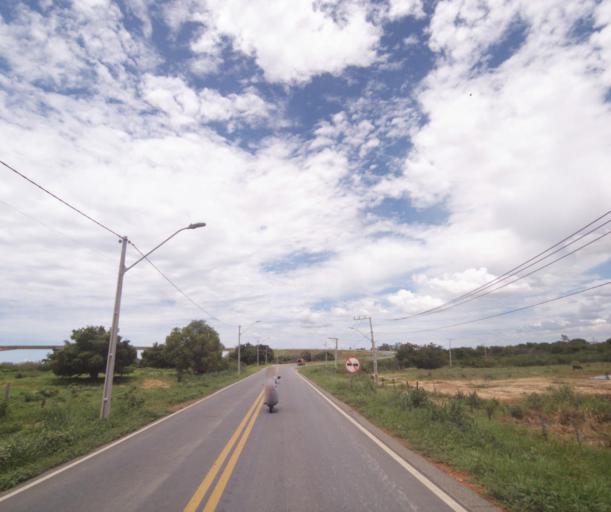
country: BR
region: Bahia
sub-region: Carinhanha
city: Carinhanha
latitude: -14.3303
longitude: -43.7681
